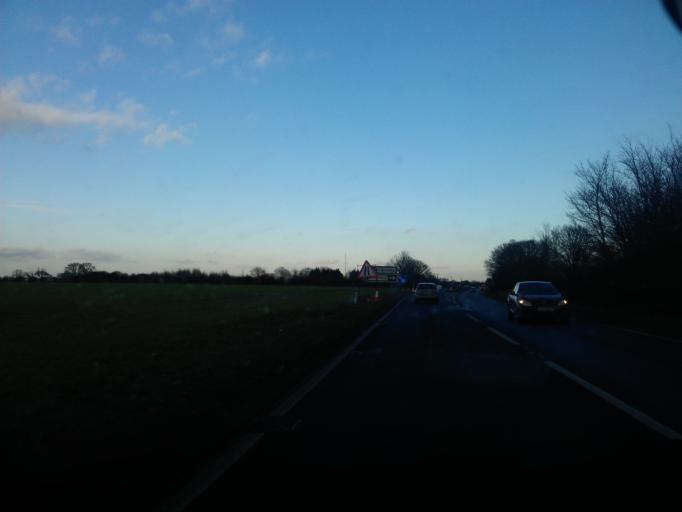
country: GB
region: England
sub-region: Essex
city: Great Bentley
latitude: 51.8939
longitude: 1.0662
